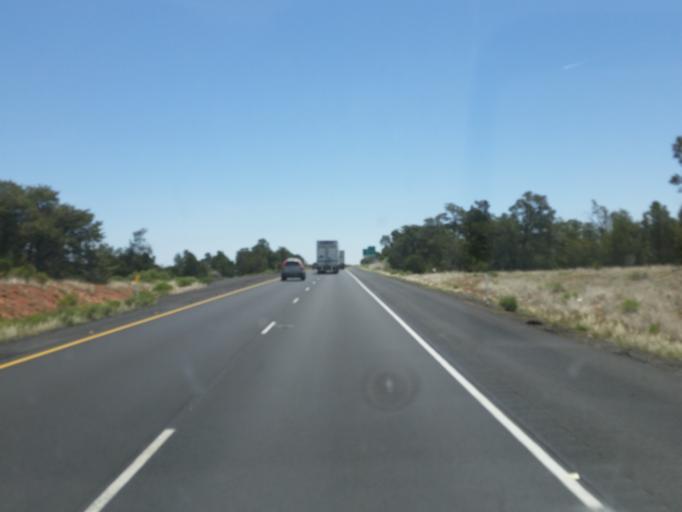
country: US
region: Arizona
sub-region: Coconino County
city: Flagstaff
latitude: 35.2025
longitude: -111.4830
